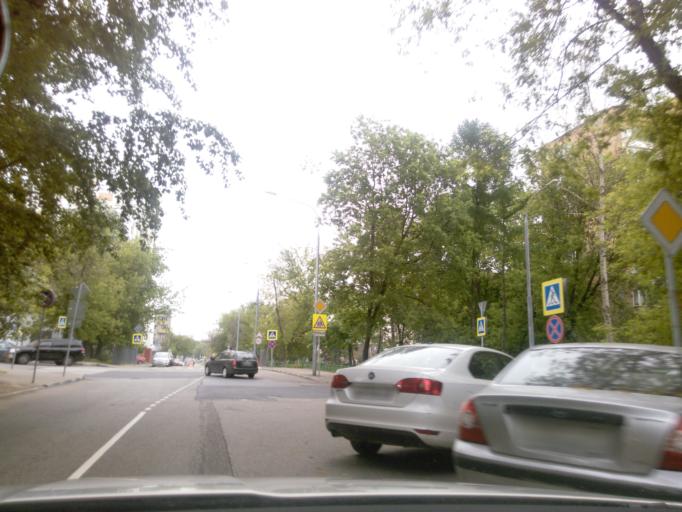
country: RU
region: Moscow
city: Taganskiy
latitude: 55.7361
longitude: 37.6828
